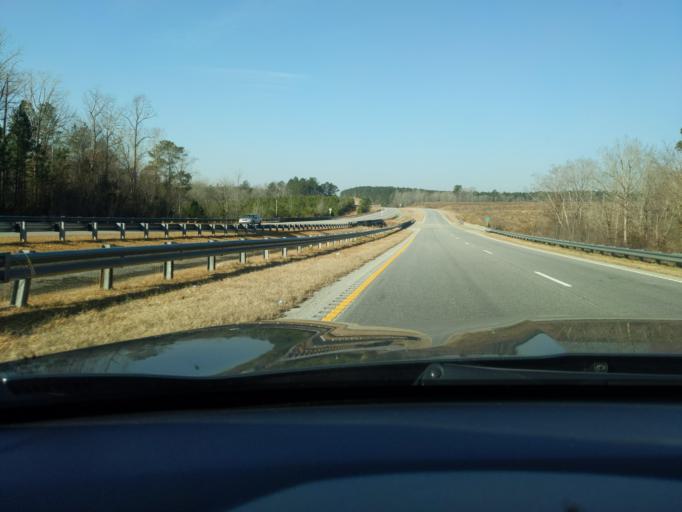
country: US
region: South Carolina
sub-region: Abbeville County
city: Abbeville
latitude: 34.1132
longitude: -82.4764
